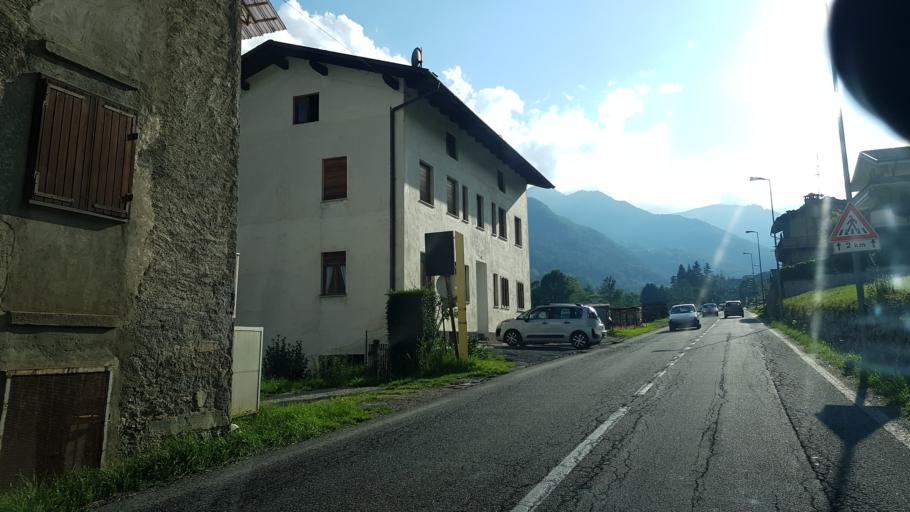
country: IT
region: Piedmont
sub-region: Provincia di Cuneo
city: Sampeyre
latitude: 44.5778
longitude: 7.2029
